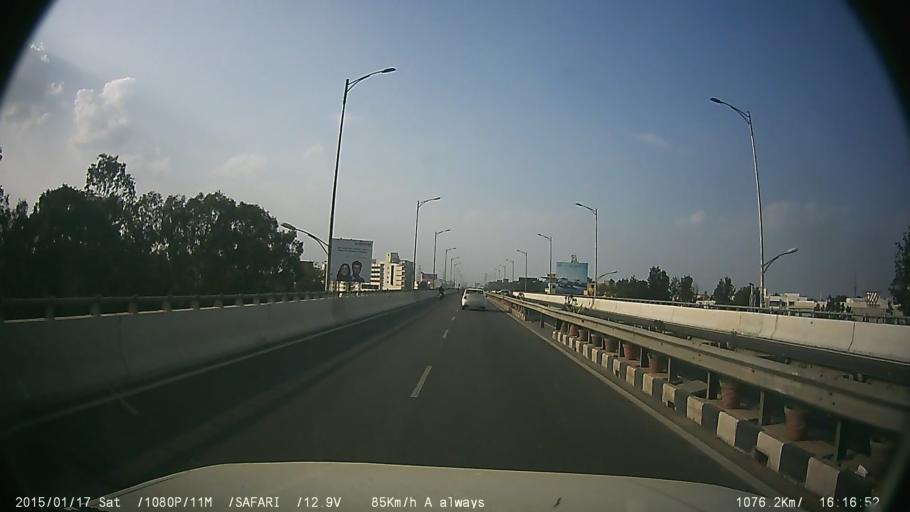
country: IN
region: Karnataka
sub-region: Bangalore Urban
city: Bangalore
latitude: 12.8656
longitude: 77.6567
